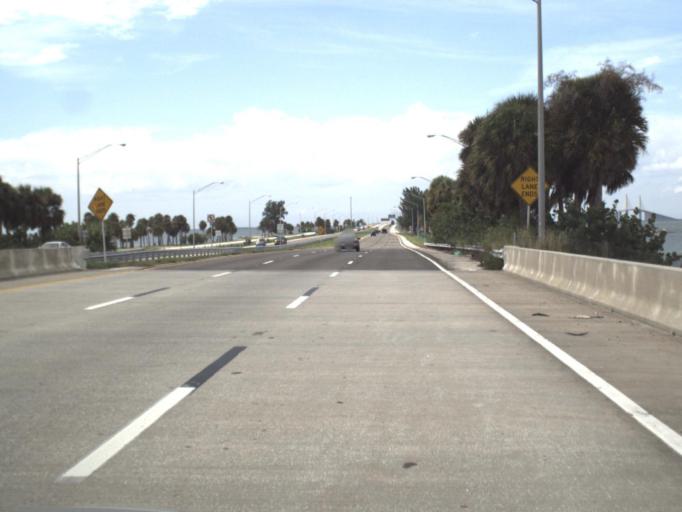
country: US
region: Florida
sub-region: Manatee County
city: Memphis
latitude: 27.5870
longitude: -82.6205
